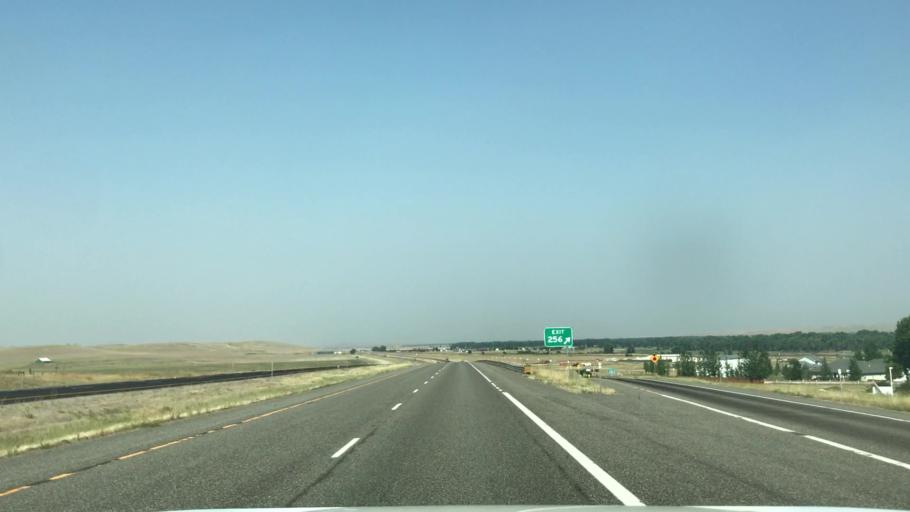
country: US
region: Montana
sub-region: Cascade County
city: Sun Prairie
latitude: 47.2774
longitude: -111.7037
